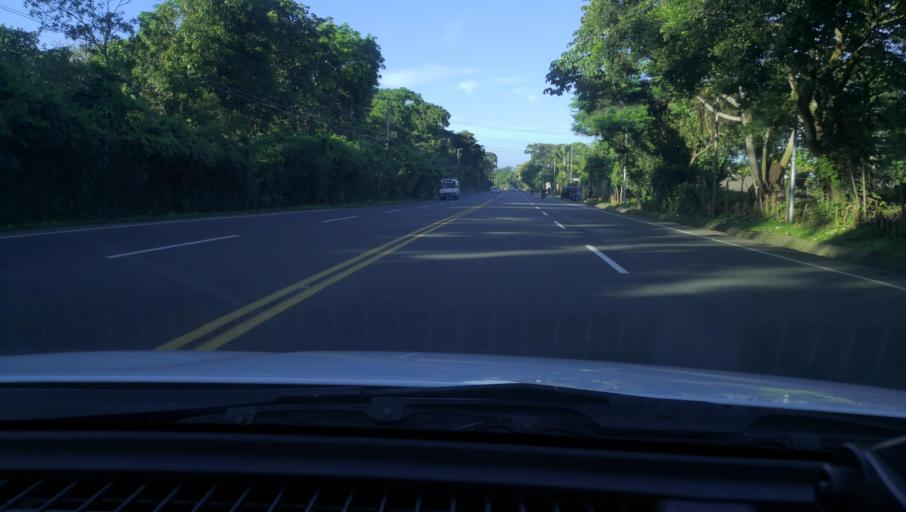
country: NI
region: Carazo
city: Diriamba
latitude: 11.8796
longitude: -86.2365
